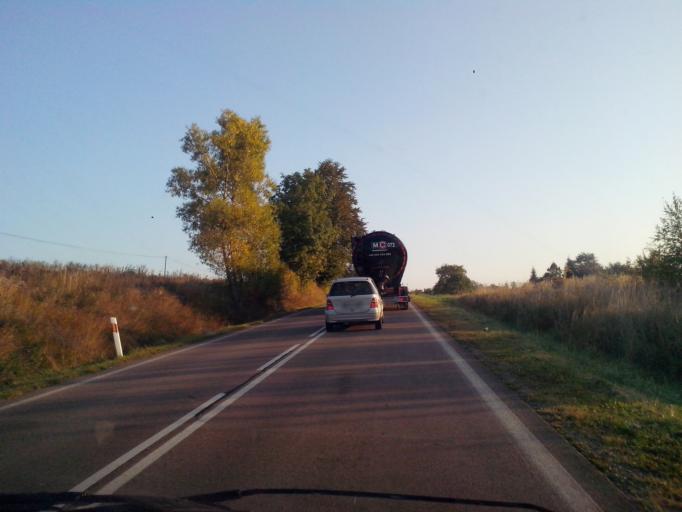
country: PL
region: Subcarpathian Voivodeship
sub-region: Powiat brzozowski
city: Wesola
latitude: 49.8204
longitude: 22.0534
